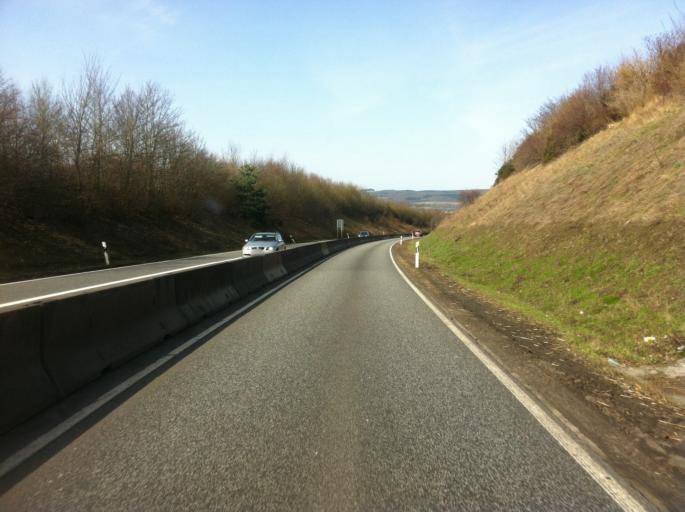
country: DE
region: Rheinland-Pfalz
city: Gering
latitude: 50.2922
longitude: 7.2440
